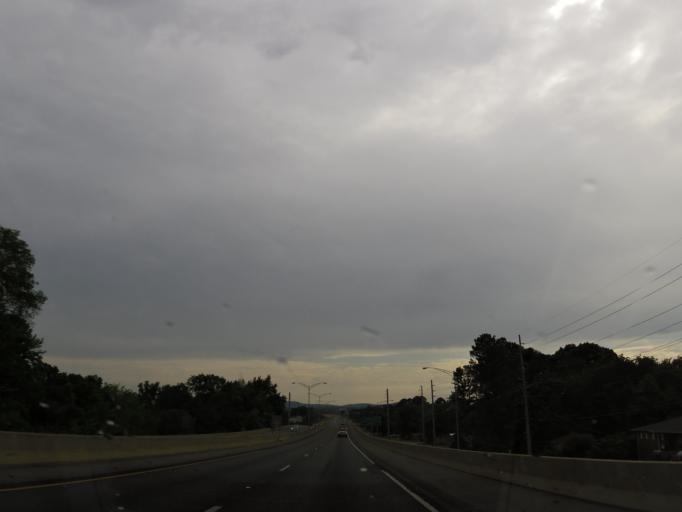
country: US
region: Alabama
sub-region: Madison County
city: Huntsville
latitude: 34.7567
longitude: -86.5669
